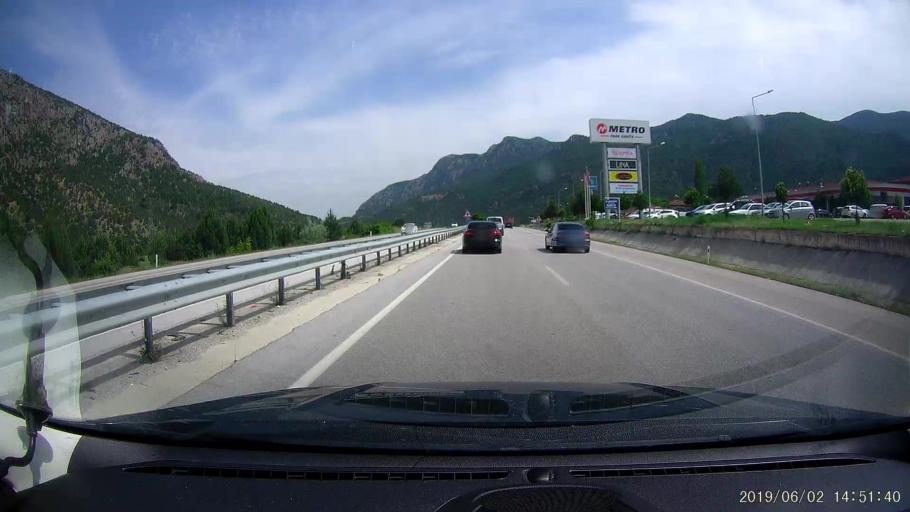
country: TR
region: Corum
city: Kargi
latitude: 41.0563
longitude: 34.5431
